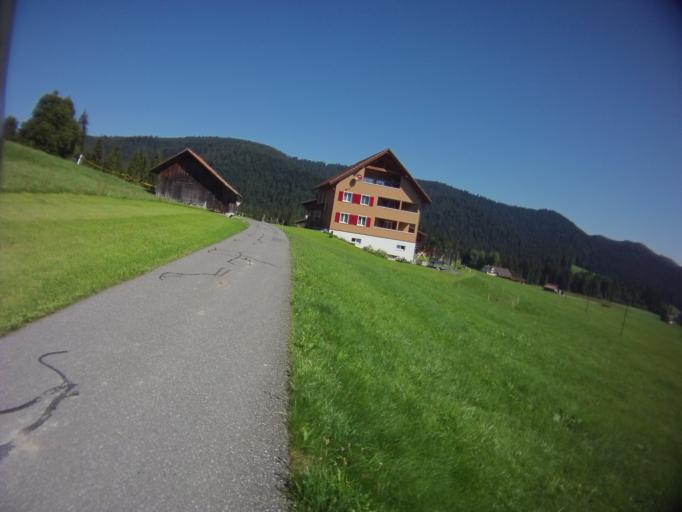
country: CH
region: Schwyz
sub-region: Bezirk Schwyz
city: Rothenthurm
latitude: 47.1435
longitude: 8.6832
